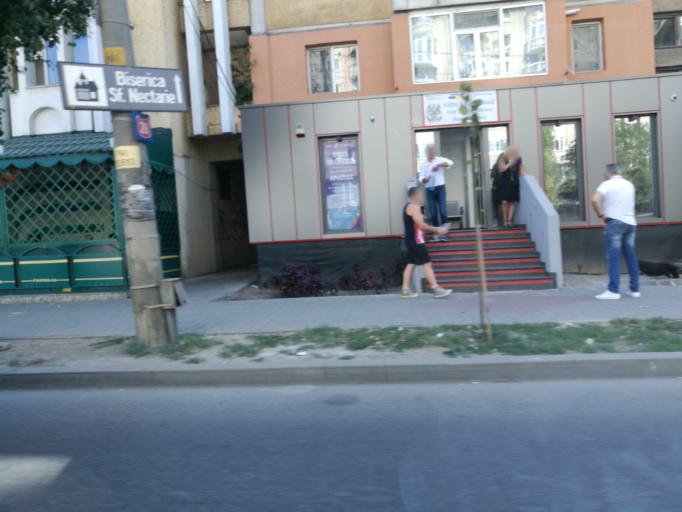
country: RO
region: Iasi
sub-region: Municipiul Iasi
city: Iasi
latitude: 47.1669
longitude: 27.5695
